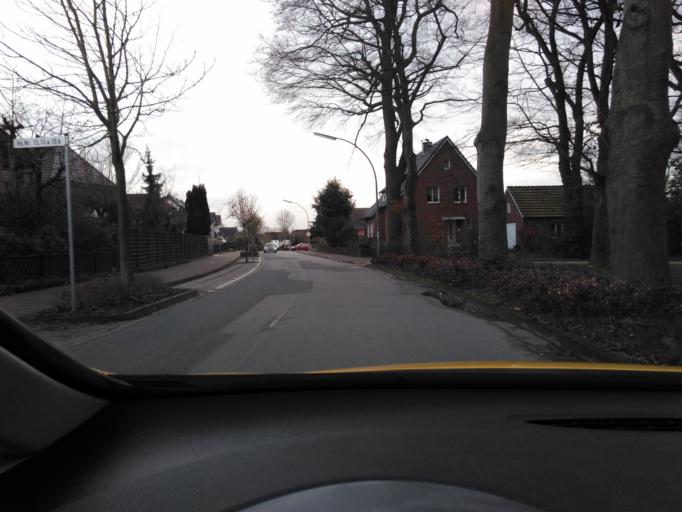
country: DE
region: North Rhine-Westphalia
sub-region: Regierungsbezirk Detmold
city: Verl
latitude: 51.8770
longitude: 8.5086
